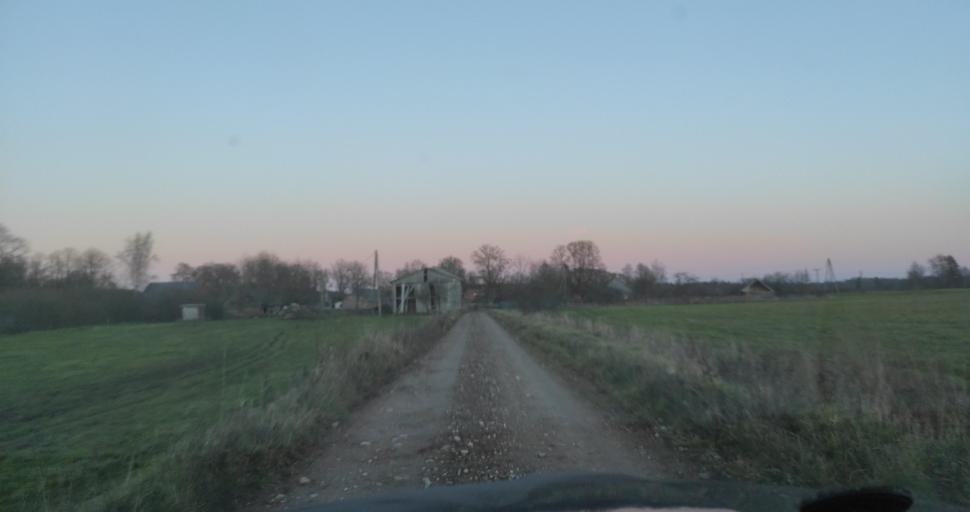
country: LV
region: Dundaga
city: Dundaga
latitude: 57.3741
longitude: 22.2270
